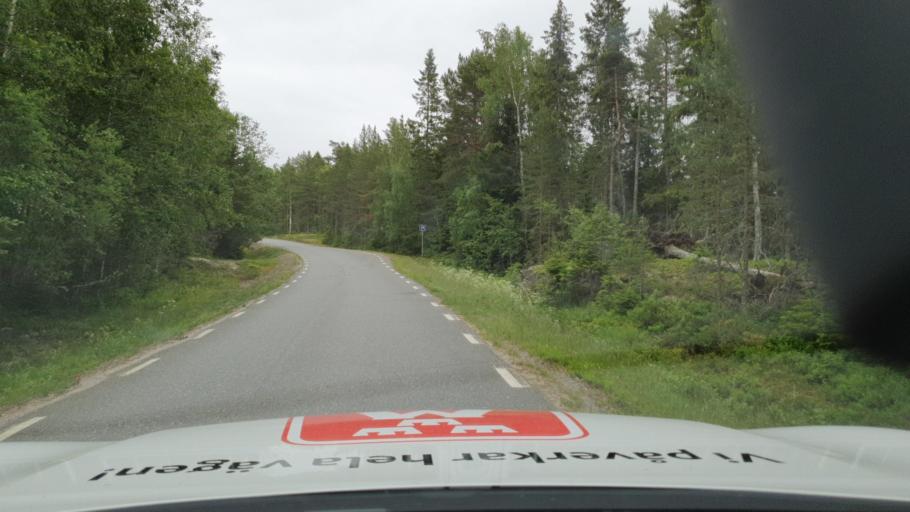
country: SE
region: Vaesterbotten
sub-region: Nordmalings Kommun
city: Nordmaling
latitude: 63.4338
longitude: 19.4735
